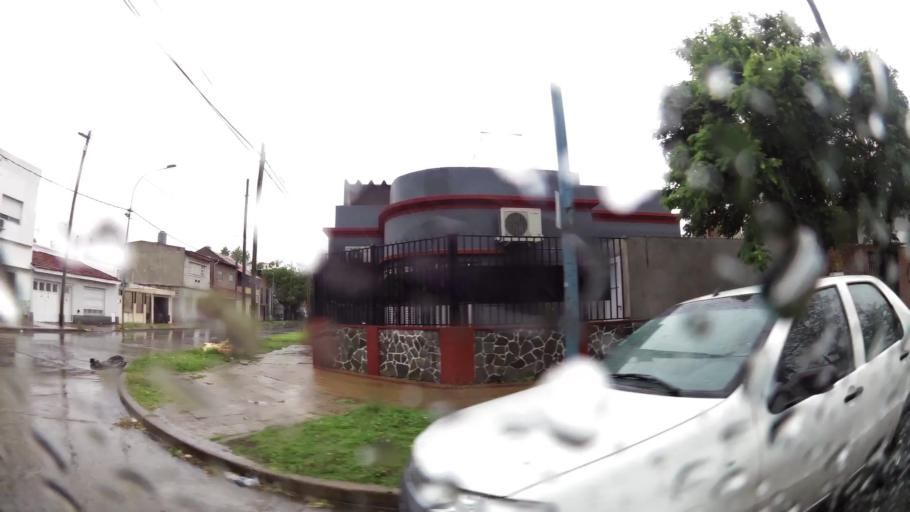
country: AR
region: Buenos Aires
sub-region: Partido de Lanus
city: Lanus
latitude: -34.7065
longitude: -58.4071
